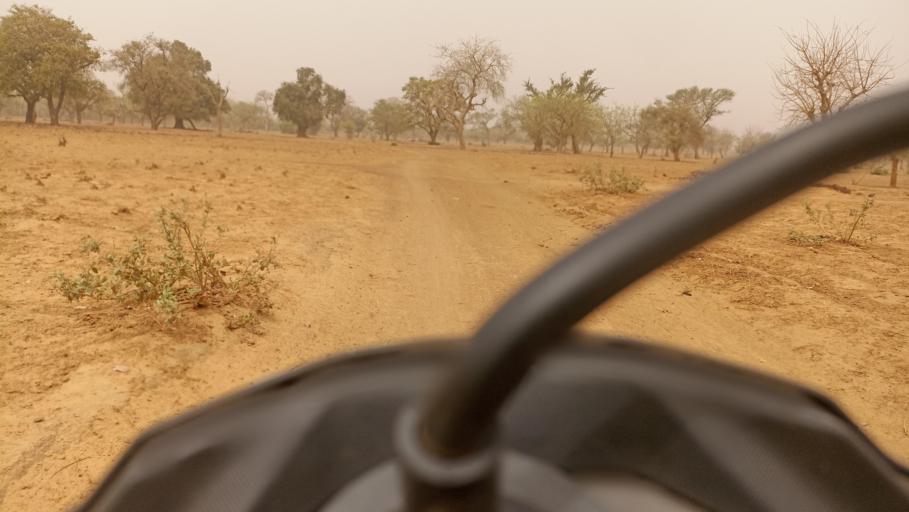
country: BF
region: Nord
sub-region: Province du Zondoma
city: Gourcy
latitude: 13.2499
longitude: -2.6023
